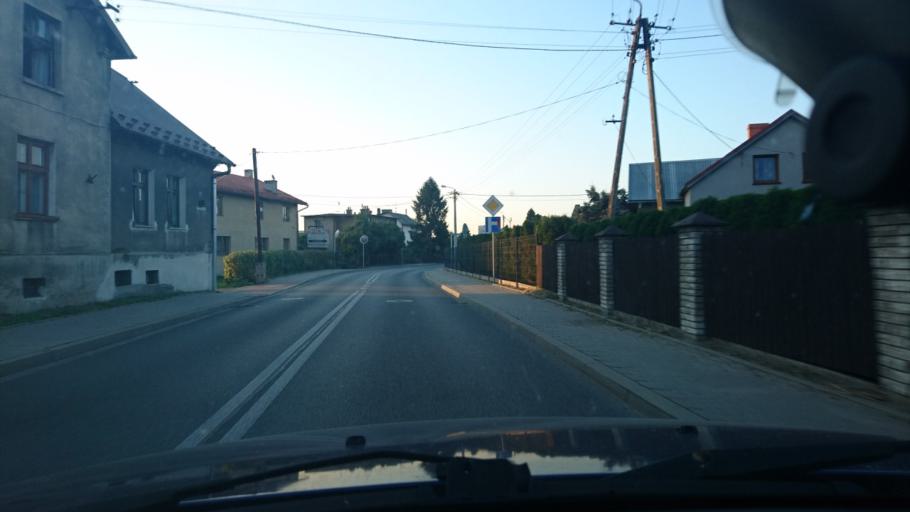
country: PL
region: Silesian Voivodeship
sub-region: Bielsko-Biala
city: Bielsko-Biala
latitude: 49.8513
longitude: 19.0505
